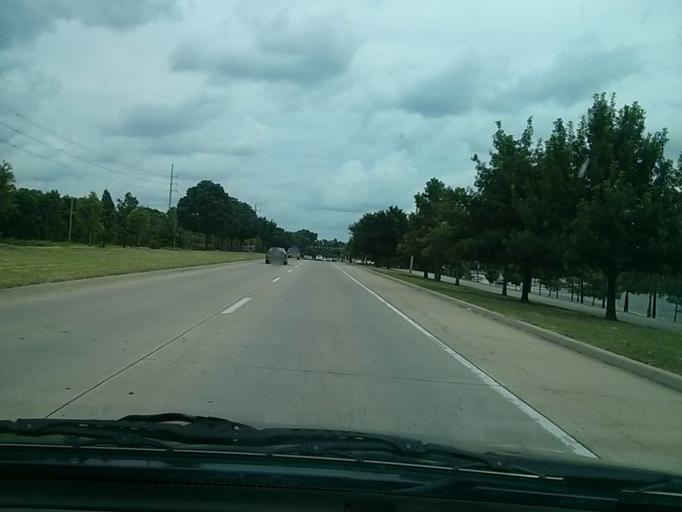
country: US
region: Oklahoma
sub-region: Tulsa County
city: Jenks
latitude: 36.0404
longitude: -95.9608
